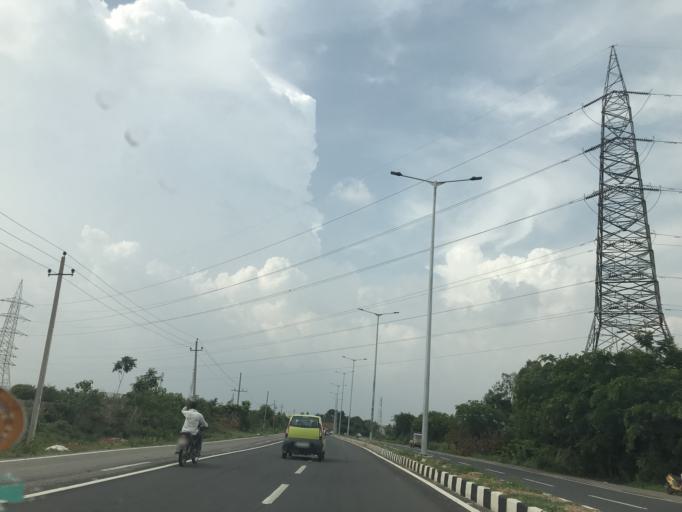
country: IN
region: Karnataka
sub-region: Bangalore Rural
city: Devanhalli
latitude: 13.1657
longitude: 77.6872
